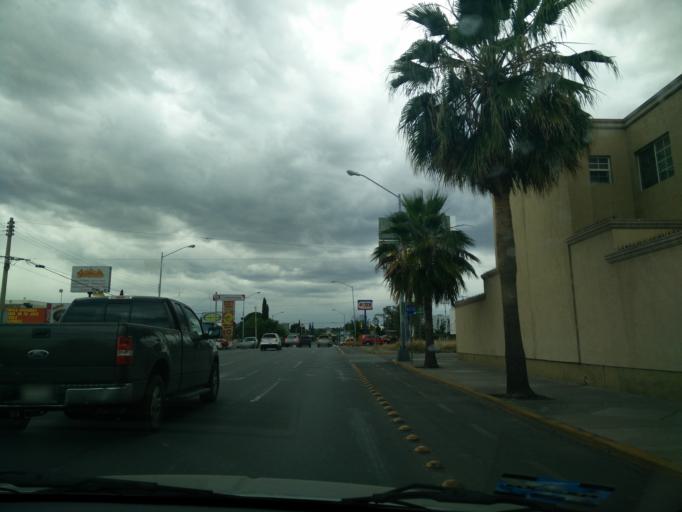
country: MX
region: Chihuahua
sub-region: Chihuahua
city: Chihuahua
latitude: 28.6499
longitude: -106.0873
